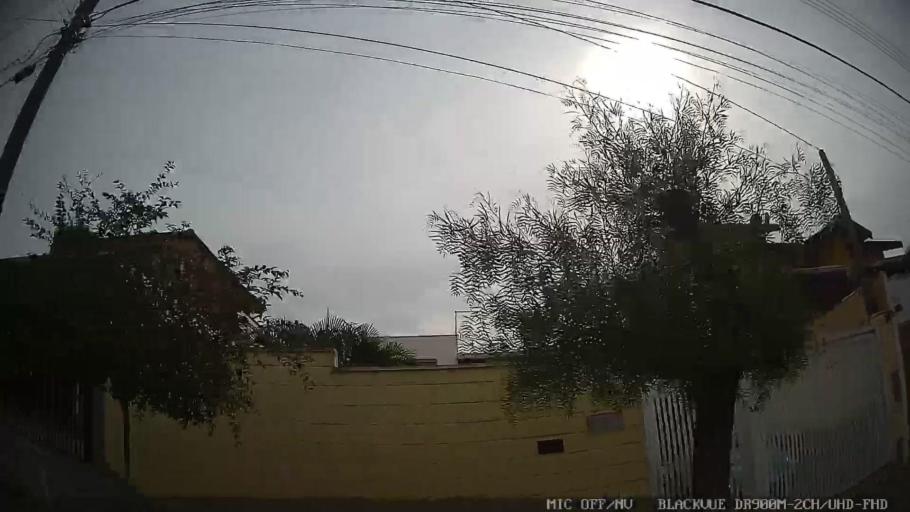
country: BR
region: Sao Paulo
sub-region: Indaiatuba
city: Indaiatuba
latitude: -23.0817
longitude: -47.2268
